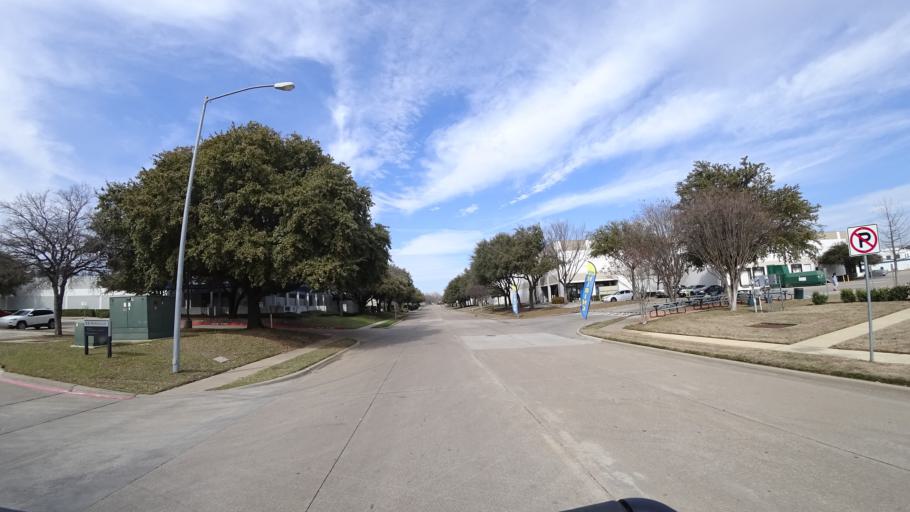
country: US
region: Texas
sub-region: Denton County
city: Lewisville
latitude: 33.0247
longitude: -96.9789
